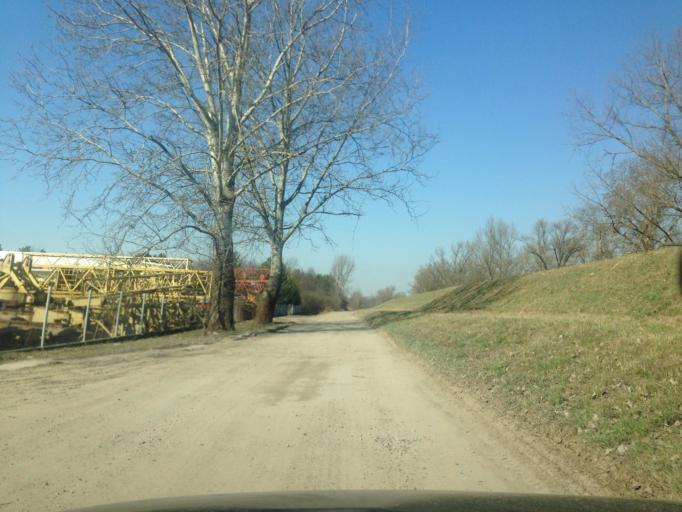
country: PL
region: Masovian Voivodeship
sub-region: Warszawa
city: Wawer
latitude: 52.1405
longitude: 21.1581
